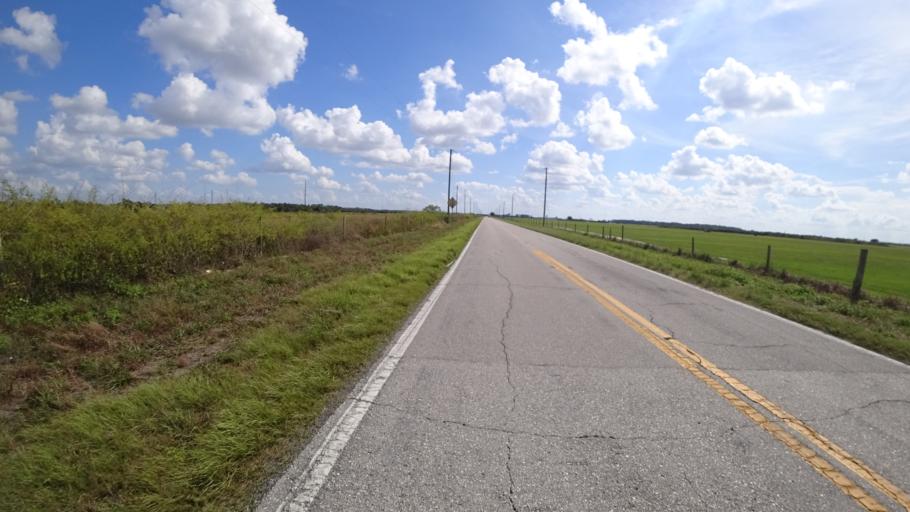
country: US
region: Florida
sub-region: Hardee County
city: Wauchula
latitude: 27.5334
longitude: -82.0781
